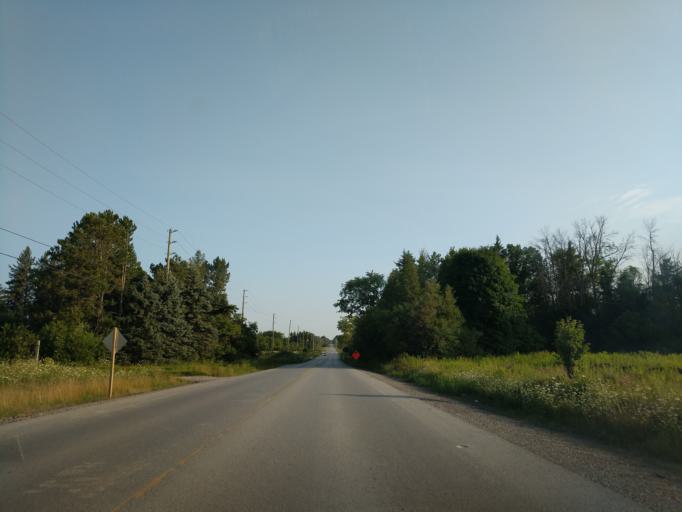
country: CA
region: Ontario
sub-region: York
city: Richmond Hill
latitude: 43.9048
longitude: -79.3973
